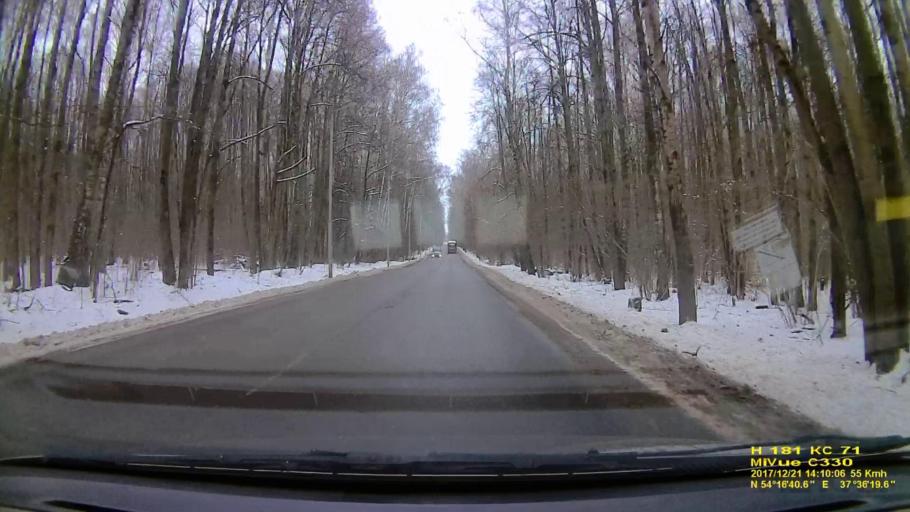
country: RU
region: Tula
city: Gorelki
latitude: 54.2781
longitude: 37.6055
